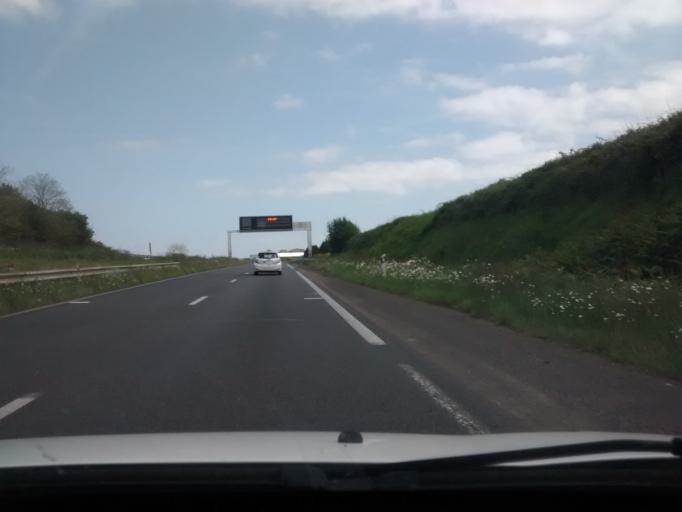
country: FR
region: Brittany
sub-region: Departement des Cotes-d'Armor
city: Tremuson
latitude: 48.5253
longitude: -2.8922
